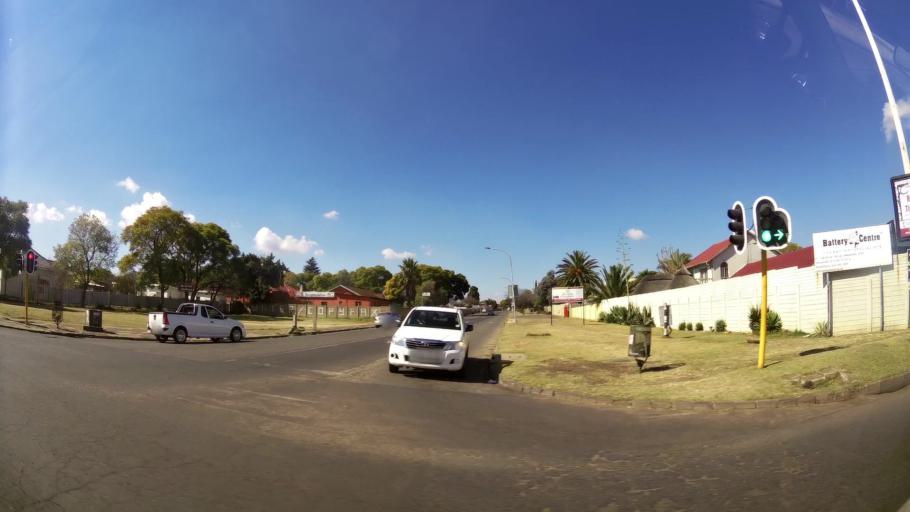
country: ZA
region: Mpumalanga
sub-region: Nkangala District Municipality
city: Witbank
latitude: -25.8803
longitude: 29.2197
